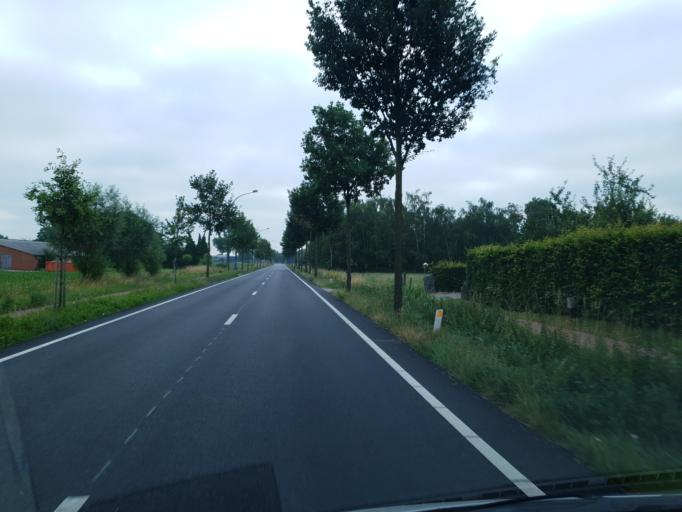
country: BE
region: Flanders
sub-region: Provincie Antwerpen
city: Hoogstraten
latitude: 51.3807
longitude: 4.7243
